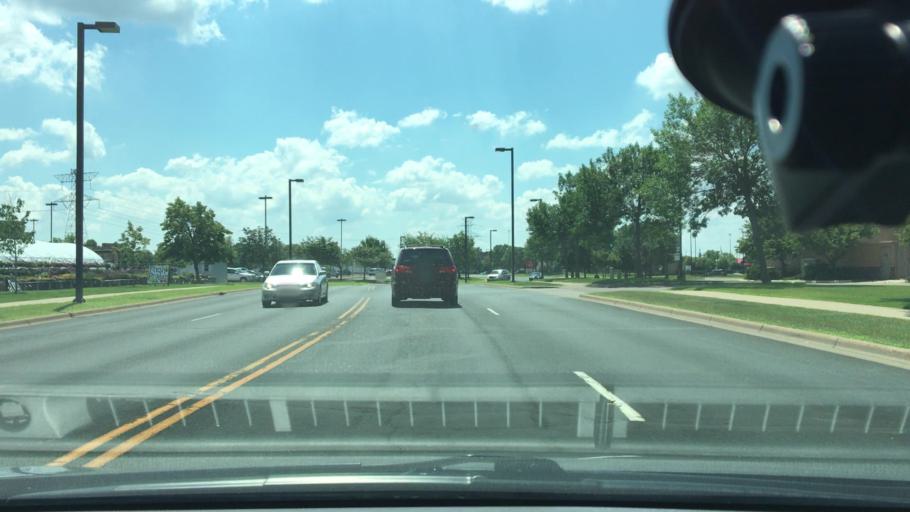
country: US
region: Minnesota
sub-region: Hennepin County
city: Maple Grove
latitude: 45.0999
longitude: -93.4495
